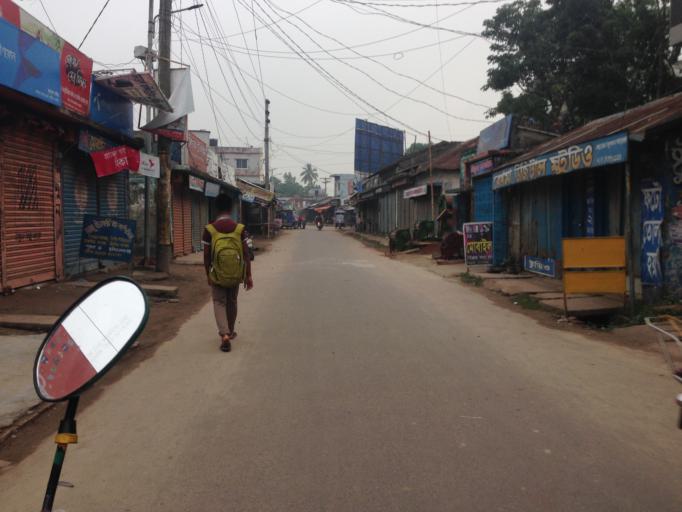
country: BD
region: Khulna
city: Kalia
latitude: 23.0403
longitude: 89.6313
